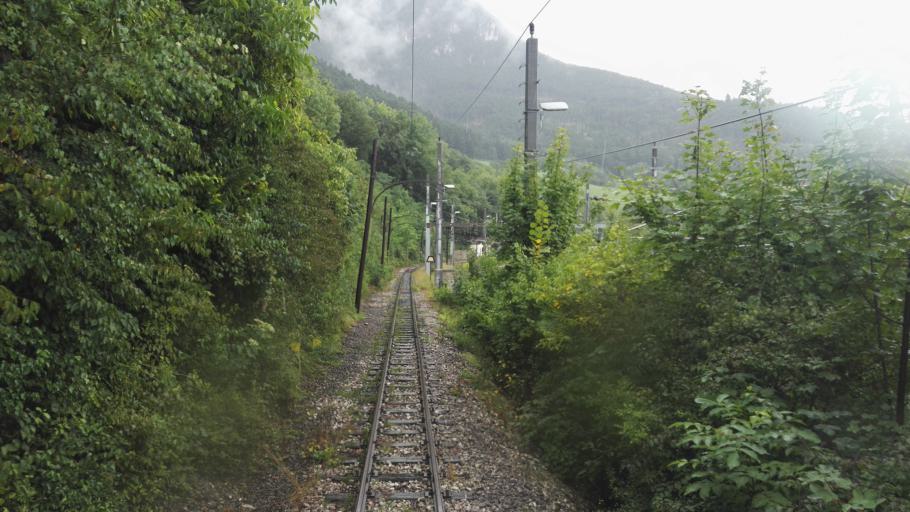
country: AT
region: Lower Austria
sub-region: Politischer Bezirk Neunkirchen
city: Payerbach
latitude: 47.6949
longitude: 15.8575
